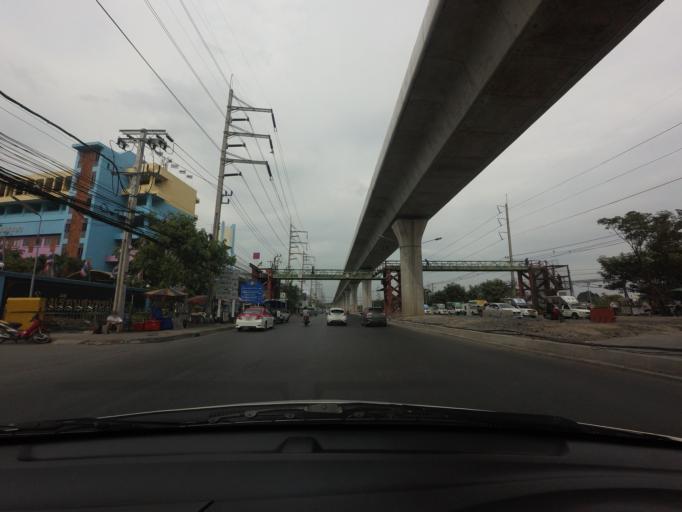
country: TH
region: Samut Prakan
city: Samut Prakan
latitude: 13.5853
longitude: 100.6082
